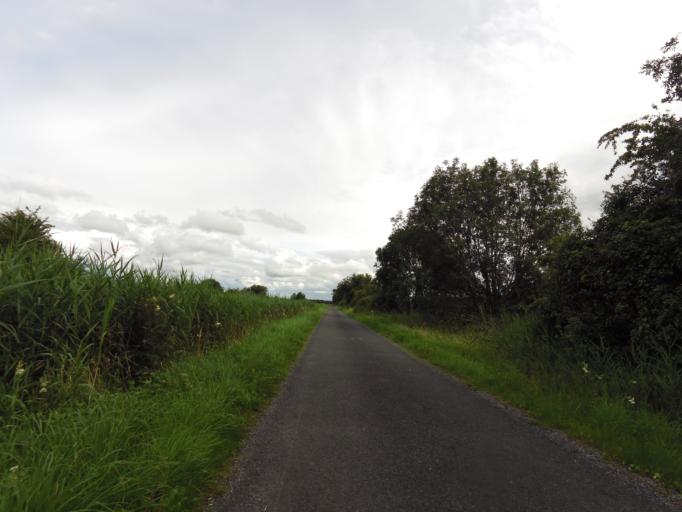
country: IE
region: Leinster
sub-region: An Longfort
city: Edgeworthstown
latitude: 53.5792
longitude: -7.5335
